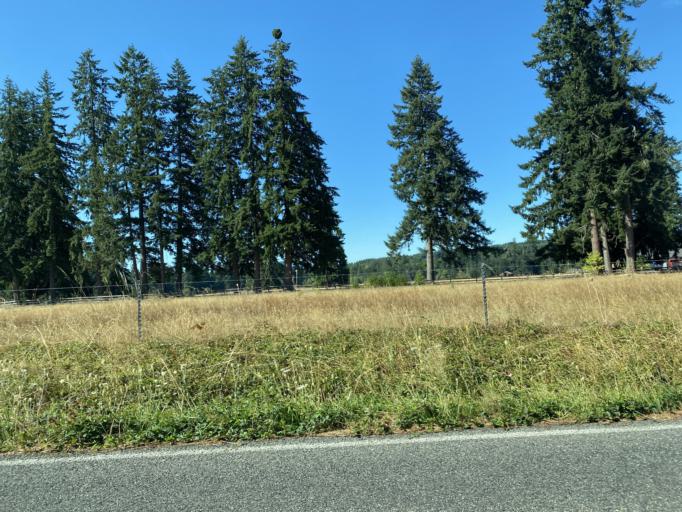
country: US
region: Washington
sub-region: Thurston County
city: Rainier
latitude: 46.8864
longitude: -122.7453
